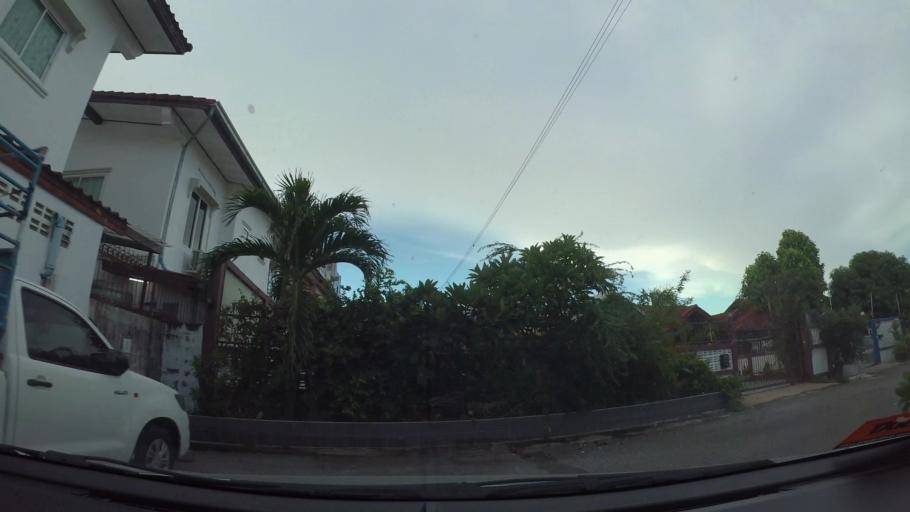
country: TH
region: Chon Buri
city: Phatthaya
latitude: 12.9119
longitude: 100.8805
